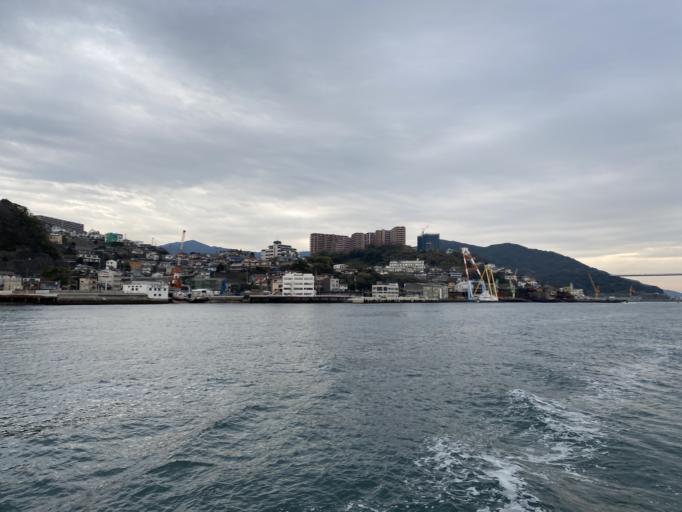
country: JP
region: Nagasaki
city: Nagasaki-shi
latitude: 32.7326
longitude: 129.8613
